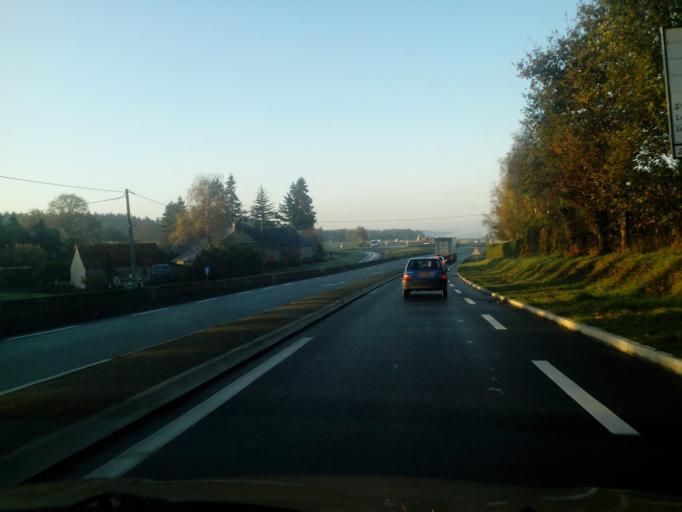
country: FR
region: Brittany
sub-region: Departement du Morbihan
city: Loyat
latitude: 47.9772
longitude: -2.3770
